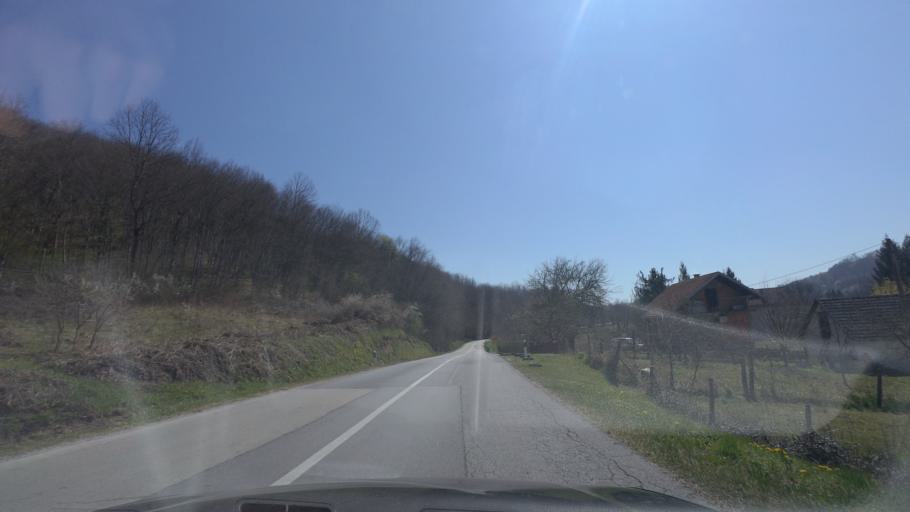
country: HR
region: Karlovacka
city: Vojnic
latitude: 45.3549
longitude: 15.6757
